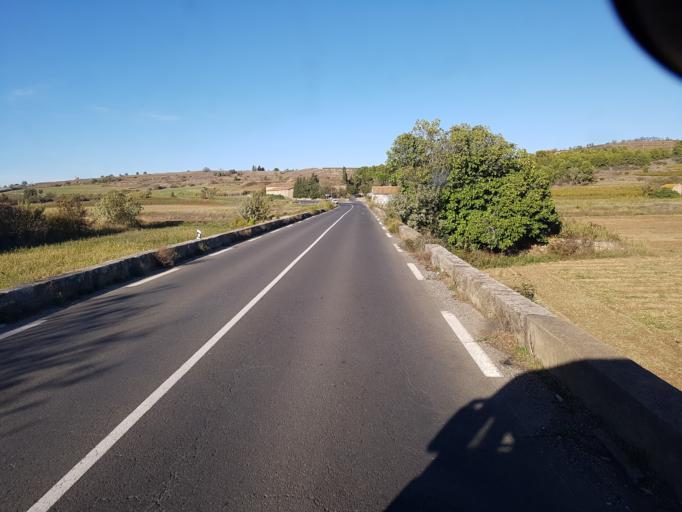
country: FR
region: Languedoc-Roussillon
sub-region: Departement de l'Aude
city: Coursan
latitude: 43.2647
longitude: 3.0801
